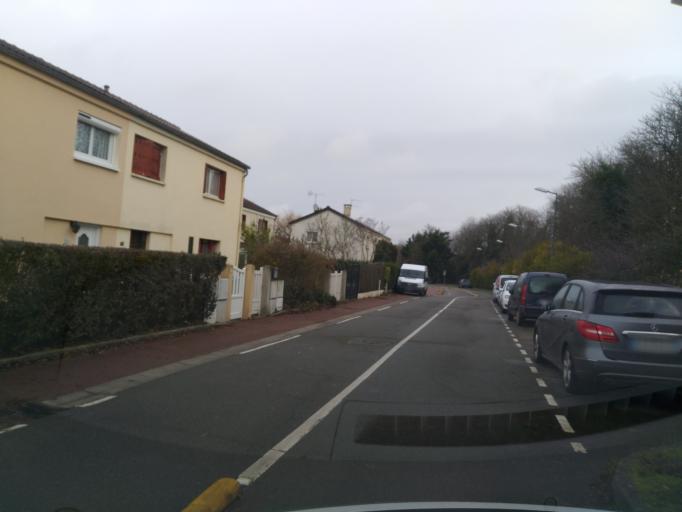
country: FR
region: Ile-de-France
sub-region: Departement des Yvelines
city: Villepreux
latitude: 48.8261
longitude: 2.0040
